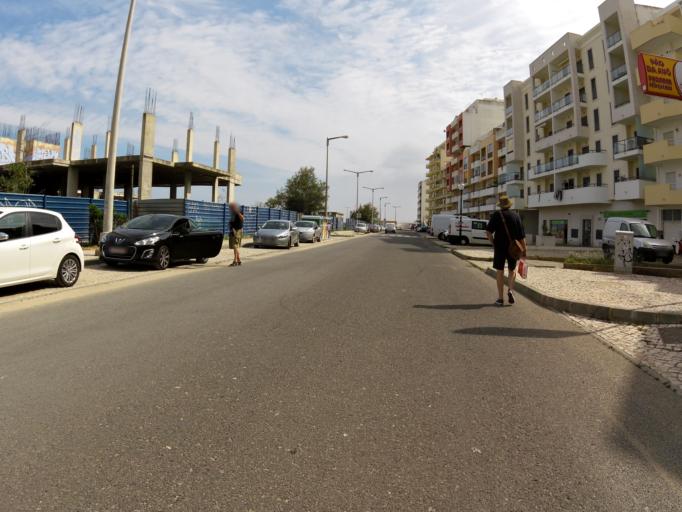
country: PT
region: Faro
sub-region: Silves
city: Armacao de Pera
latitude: 37.1032
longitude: -8.3561
